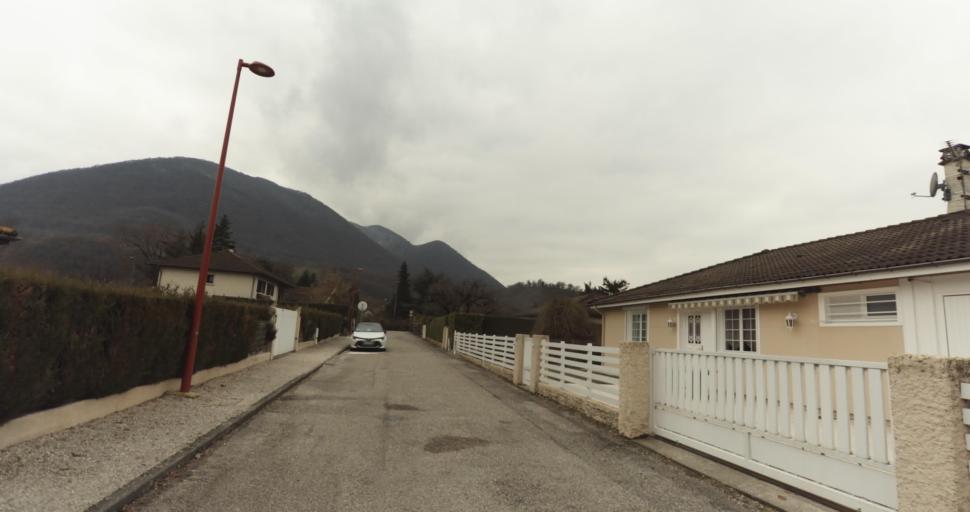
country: FR
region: Rhone-Alpes
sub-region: Departement de l'Isere
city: Vif
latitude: 45.0532
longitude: 5.6785
